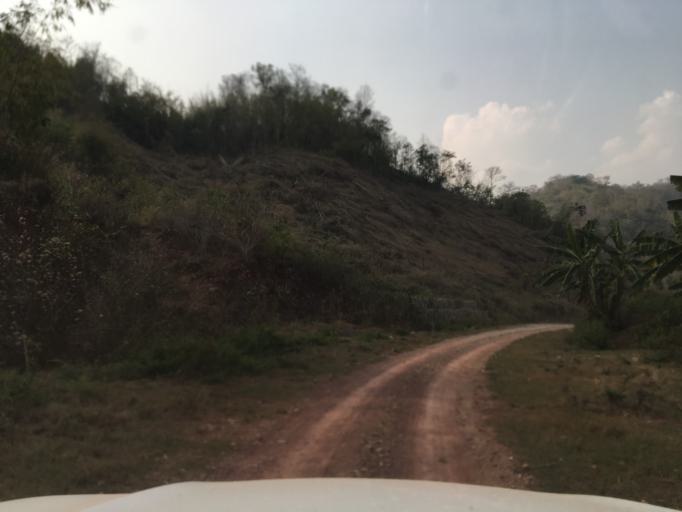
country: LA
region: Xiangkhoang
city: Phonsavan
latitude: 19.8176
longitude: 103.0024
